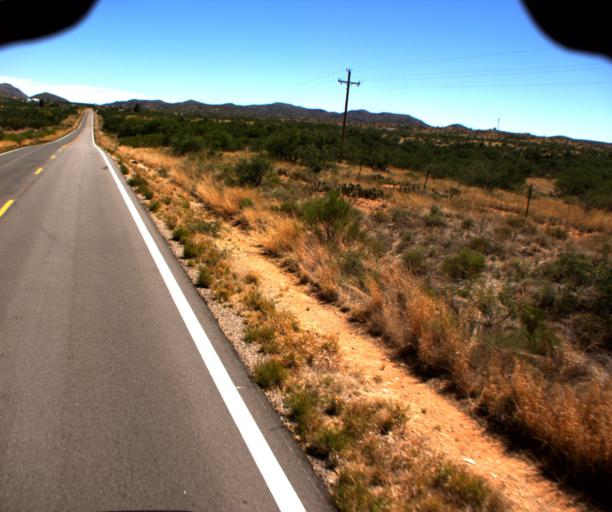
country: US
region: Arizona
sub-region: Santa Cruz County
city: Tubac
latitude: 31.5043
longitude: -111.5459
